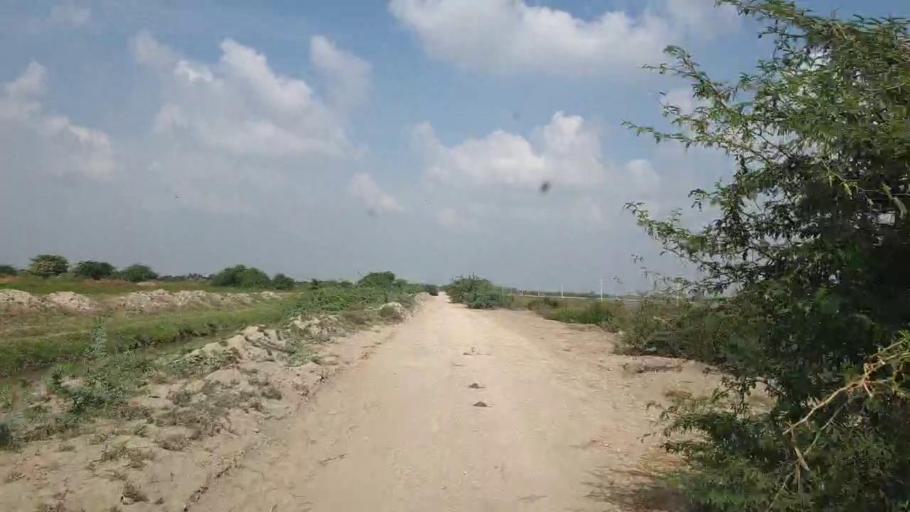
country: PK
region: Sindh
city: Badin
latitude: 24.5020
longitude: 68.6557
